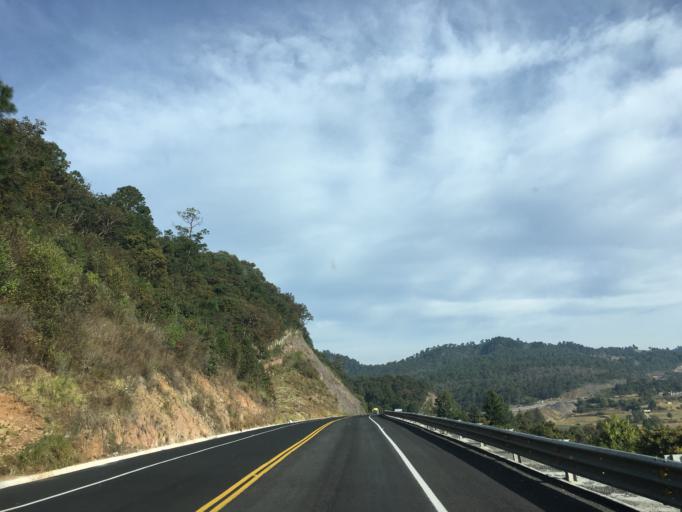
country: MX
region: Mexico
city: San Bartolo
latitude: 19.2479
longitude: -100.0667
